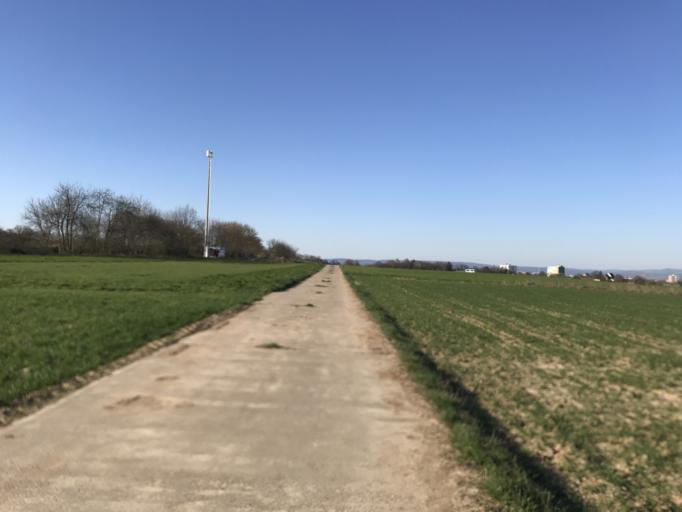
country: DE
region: Rheinland-Pfalz
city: Klein-Winternheim
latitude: 49.9512
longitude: 8.2303
